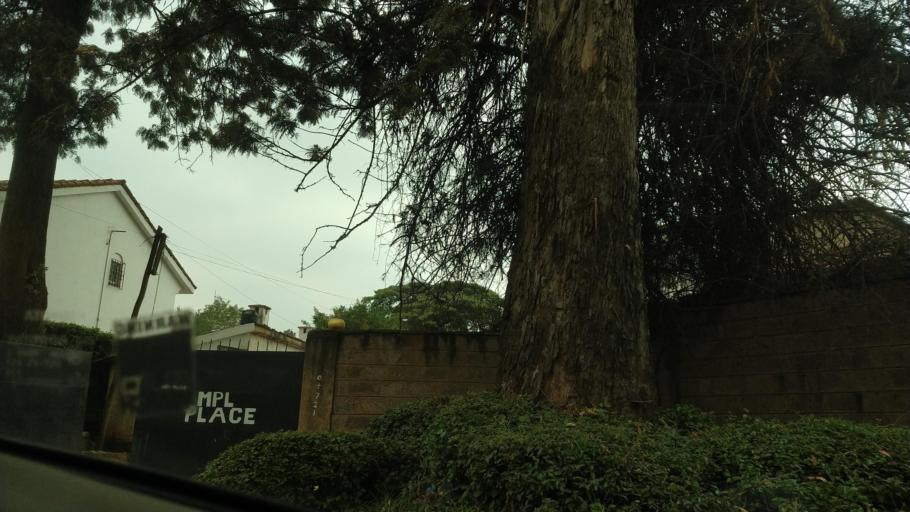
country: KE
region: Nairobi Area
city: Nairobi
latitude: -1.2933
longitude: 36.7817
